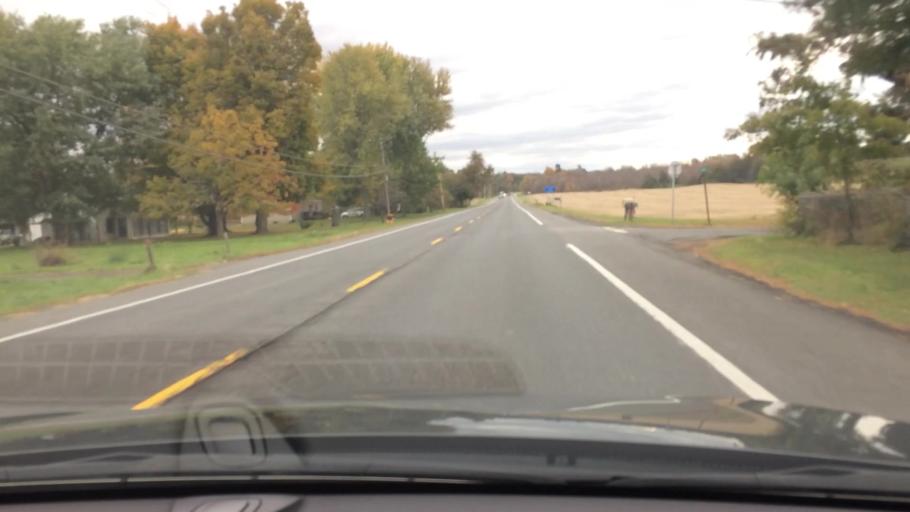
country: US
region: New York
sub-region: Columbia County
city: Oakdale
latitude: 42.1700
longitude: -73.7557
